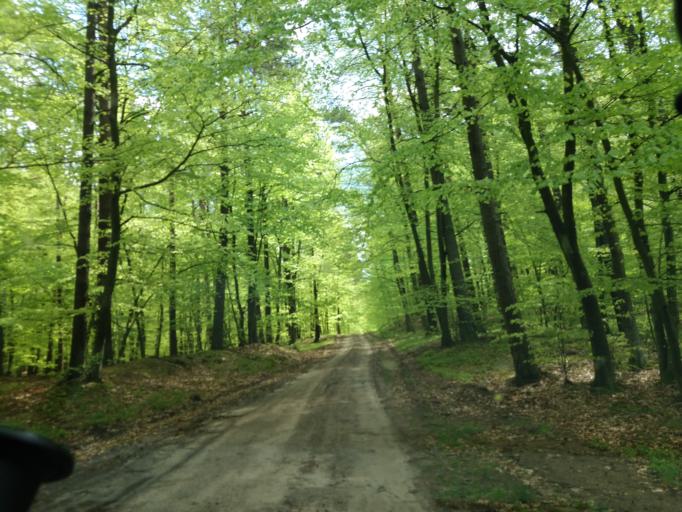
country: PL
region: West Pomeranian Voivodeship
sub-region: Powiat choszczenski
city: Drawno
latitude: 53.1444
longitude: 15.8209
